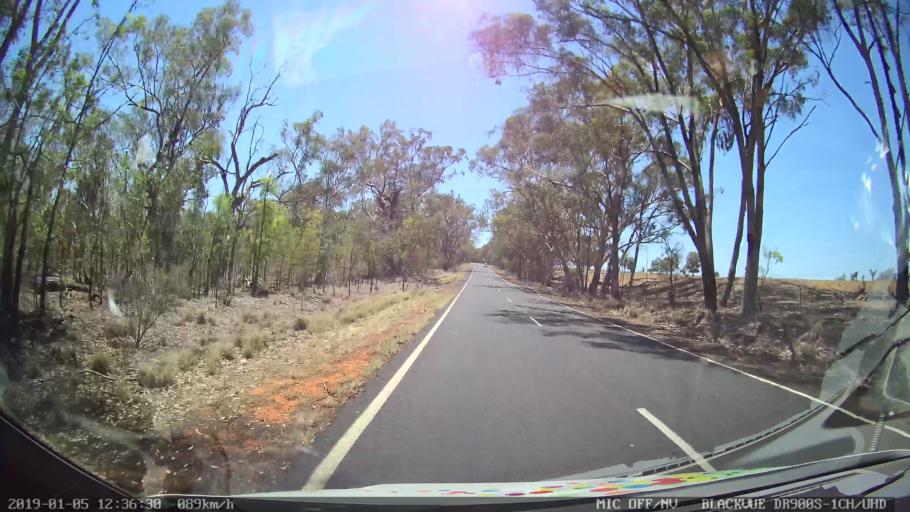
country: AU
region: New South Wales
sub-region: Warrumbungle Shire
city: Coonabarabran
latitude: -31.2070
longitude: 149.4413
